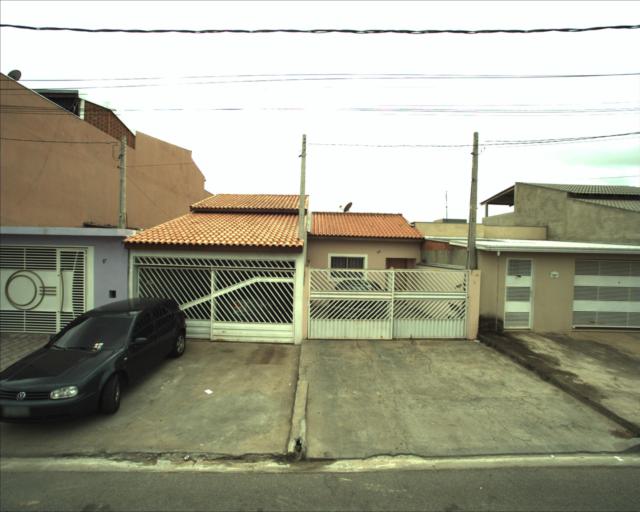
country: BR
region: Sao Paulo
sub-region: Sorocaba
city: Sorocaba
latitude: -23.4405
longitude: -47.4998
